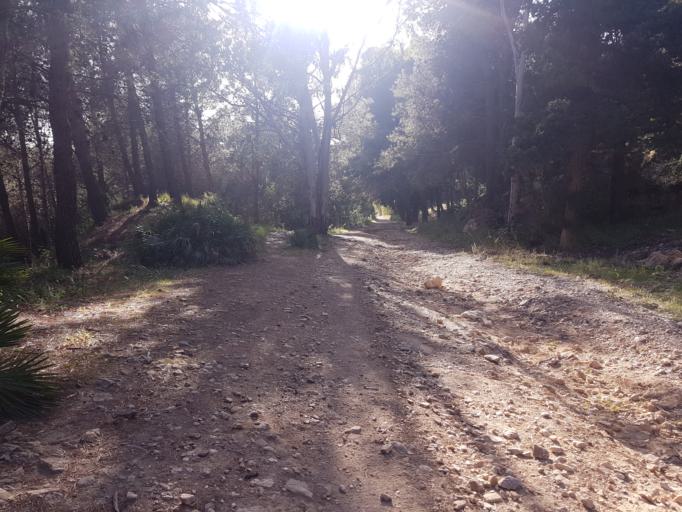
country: ES
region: Andalusia
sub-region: Provincia de Malaga
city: Marbella
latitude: 36.5306
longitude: -4.8775
